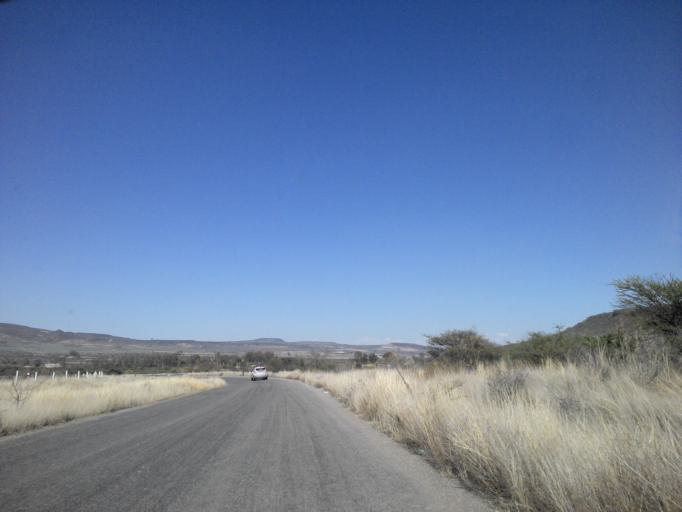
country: MX
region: Jalisco
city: San Diego de Alejandria
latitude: 20.8836
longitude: -102.0610
